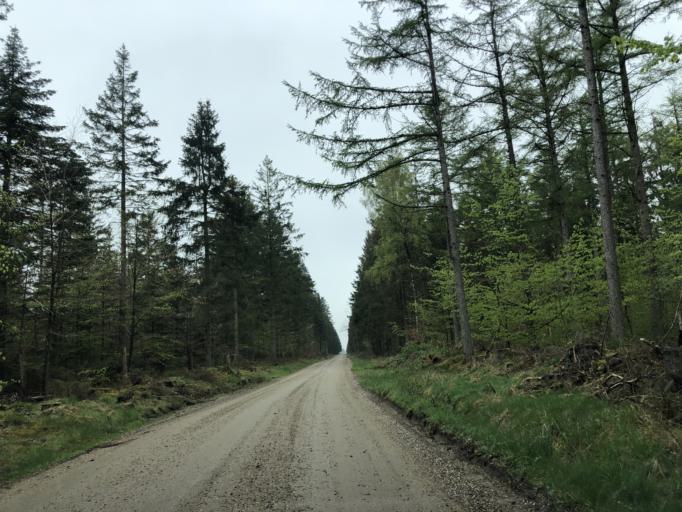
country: DK
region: Central Jutland
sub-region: Lemvig Kommune
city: Lemvig
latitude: 56.4869
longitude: 8.3568
